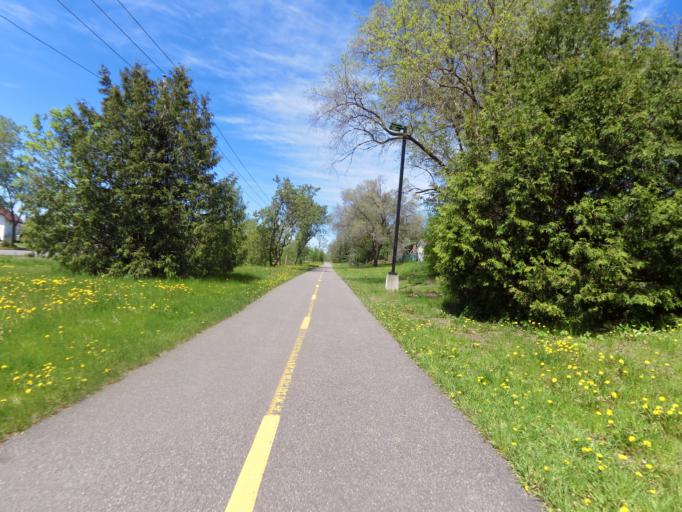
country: CA
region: Ontario
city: Bells Corners
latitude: 45.3902
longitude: -75.8445
